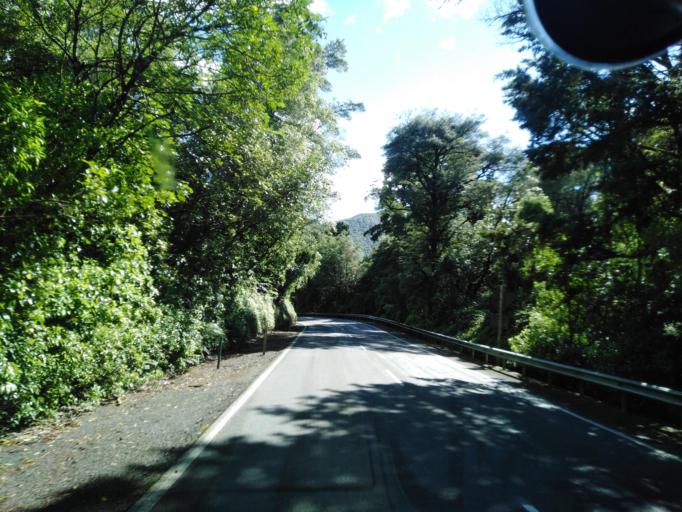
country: NZ
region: Nelson
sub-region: Nelson City
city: Nelson
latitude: -41.2970
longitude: 173.5726
